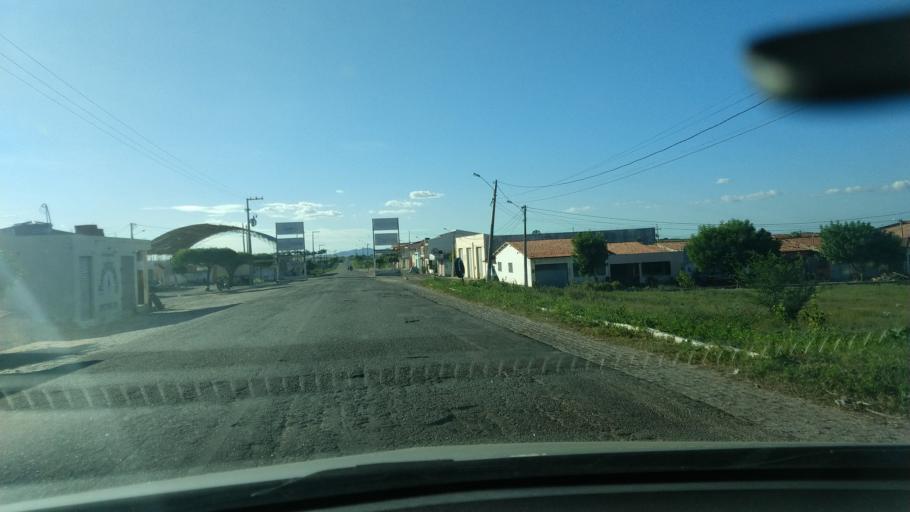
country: BR
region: Rio Grande do Norte
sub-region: Sao Jose Do Campestre
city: Sao Jose do Campestre
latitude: -6.4267
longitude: -35.6466
